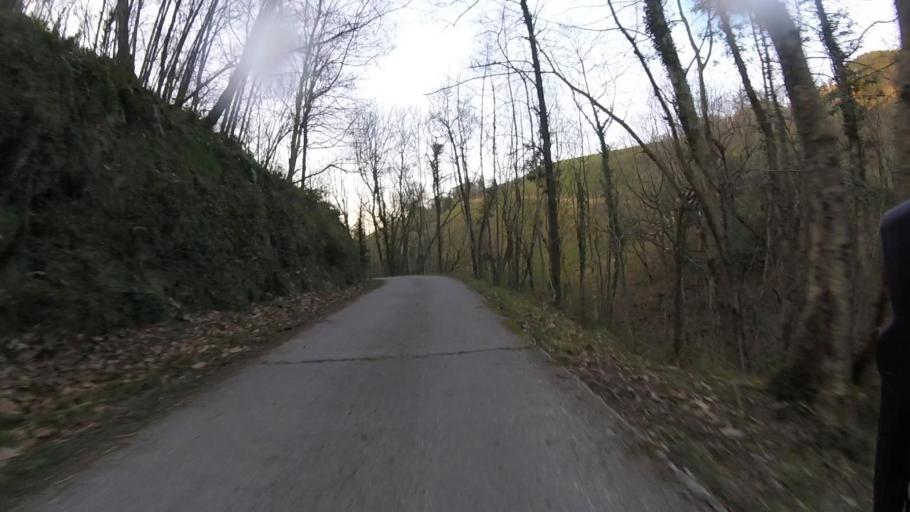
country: ES
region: Basque Country
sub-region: Provincia de Guipuzcoa
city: Errenteria
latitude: 43.2738
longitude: -1.8661
